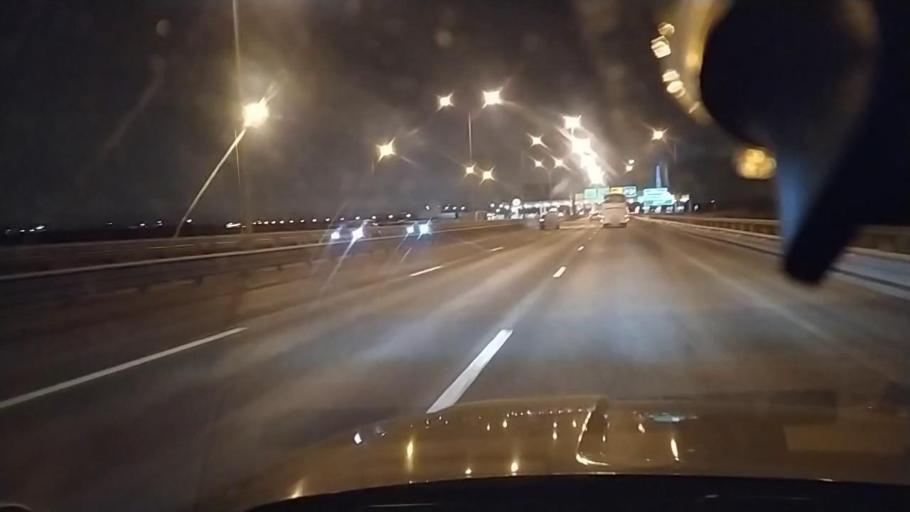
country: RU
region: St.-Petersburg
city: Ol'gino
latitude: 60.0528
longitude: 30.1471
